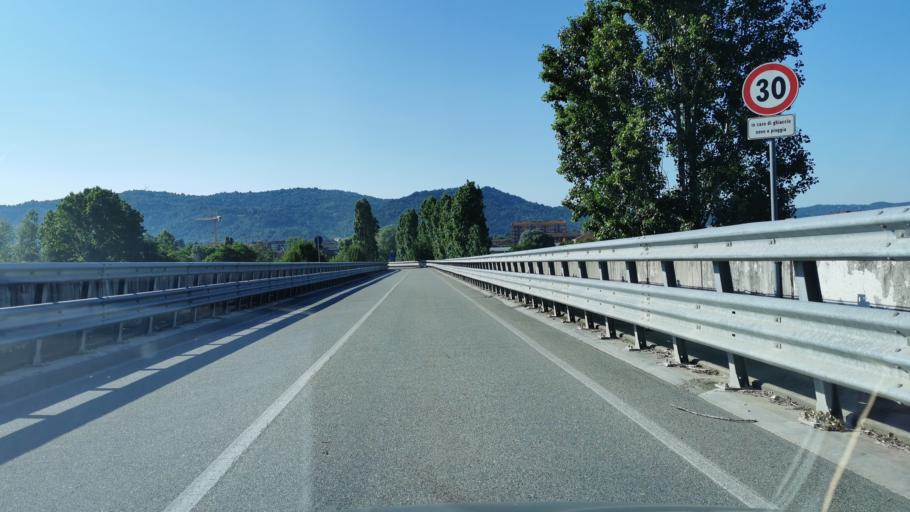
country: IT
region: Piedmont
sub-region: Provincia di Torino
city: Brandizzo
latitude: 45.1854
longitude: 7.8412
